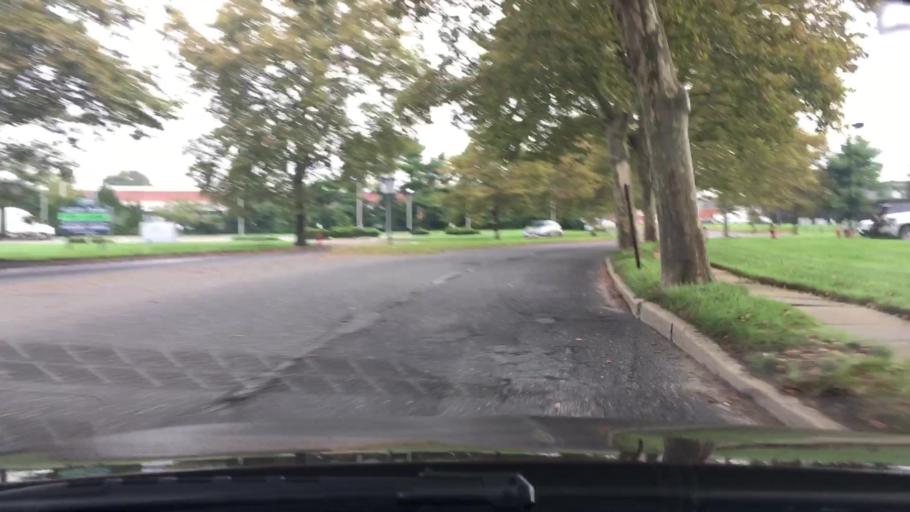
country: US
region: New York
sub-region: Suffolk County
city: Melville
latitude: 40.7772
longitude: -73.4126
